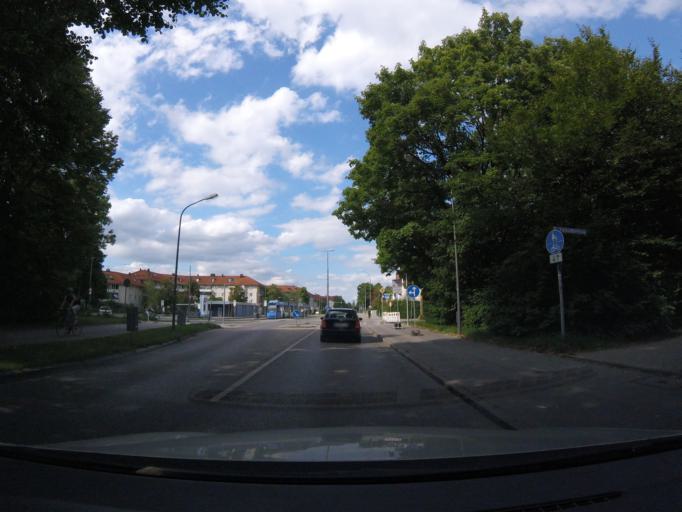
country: DE
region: Bavaria
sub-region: Upper Bavaria
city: Bogenhausen
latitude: 48.1211
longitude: 11.6421
